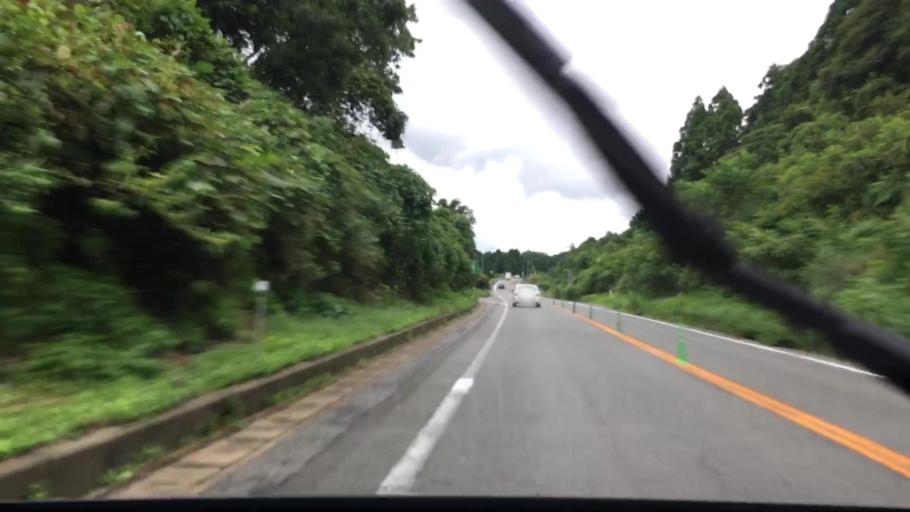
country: JP
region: Hyogo
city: Nishiwaki
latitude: 35.1017
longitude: 134.7774
